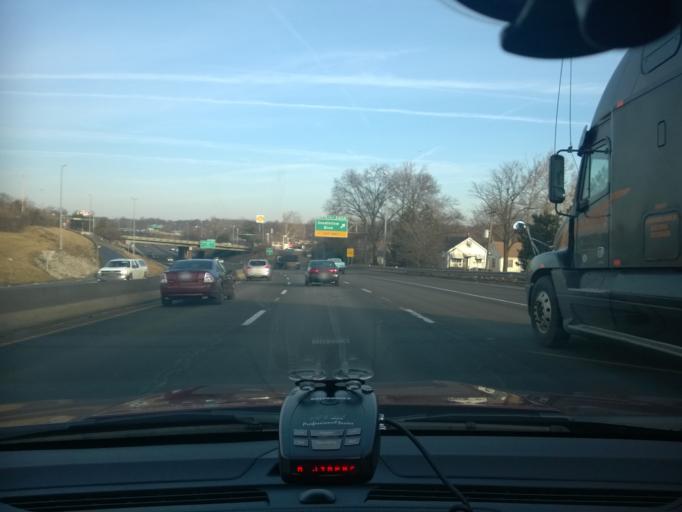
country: US
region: Missouri
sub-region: Saint Louis County
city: Pine Lawn
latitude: 38.6994
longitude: -90.2619
